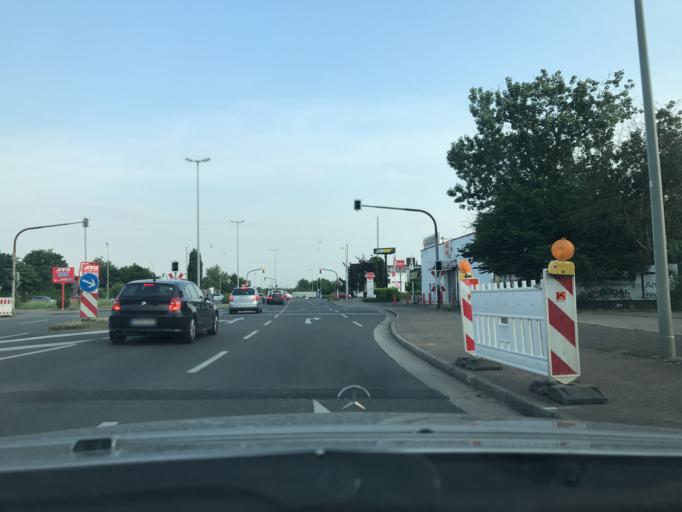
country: DE
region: North Rhine-Westphalia
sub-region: Regierungsbezirk Dusseldorf
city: Krefeld
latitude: 51.3235
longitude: 6.5933
